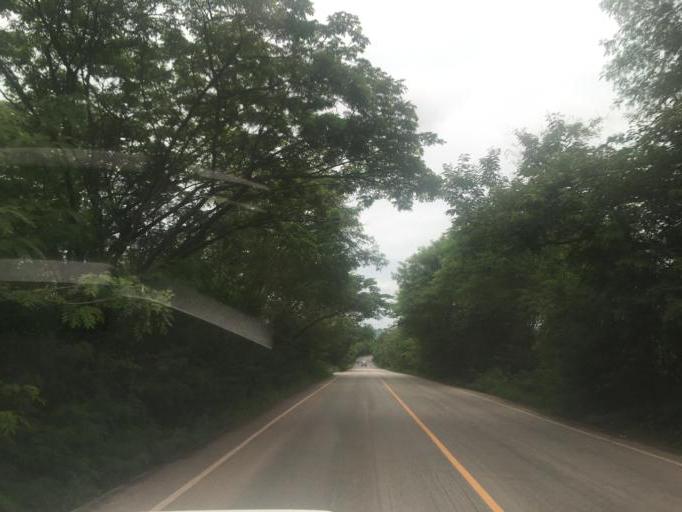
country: TH
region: Changwat Udon Thani
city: Udon Thani
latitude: 17.3179
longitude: 102.7121
